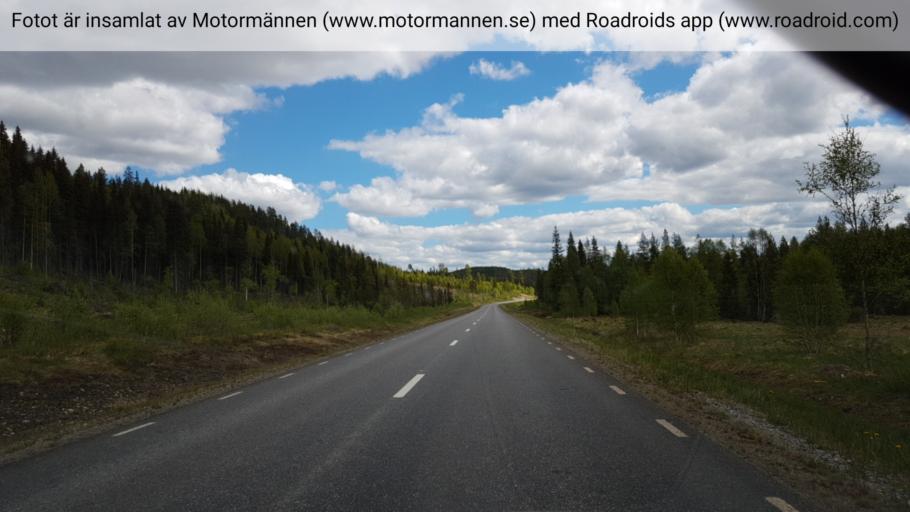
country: SE
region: Vaesterbotten
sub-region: Norsjo Kommun
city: Norsjoe
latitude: 64.8893
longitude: 19.6183
